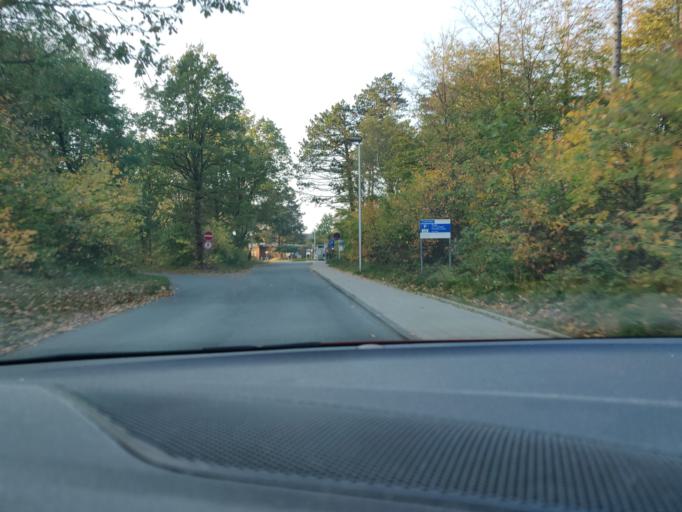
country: DE
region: Lower Saxony
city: Nordholz
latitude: 53.8635
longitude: 8.6019
